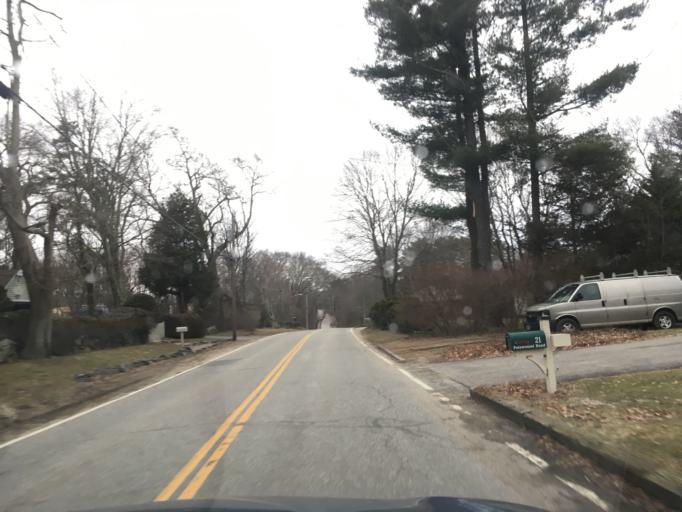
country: US
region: Rhode Island
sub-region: Kent County
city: East Greenwich
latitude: 41.6279
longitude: -71.4532
